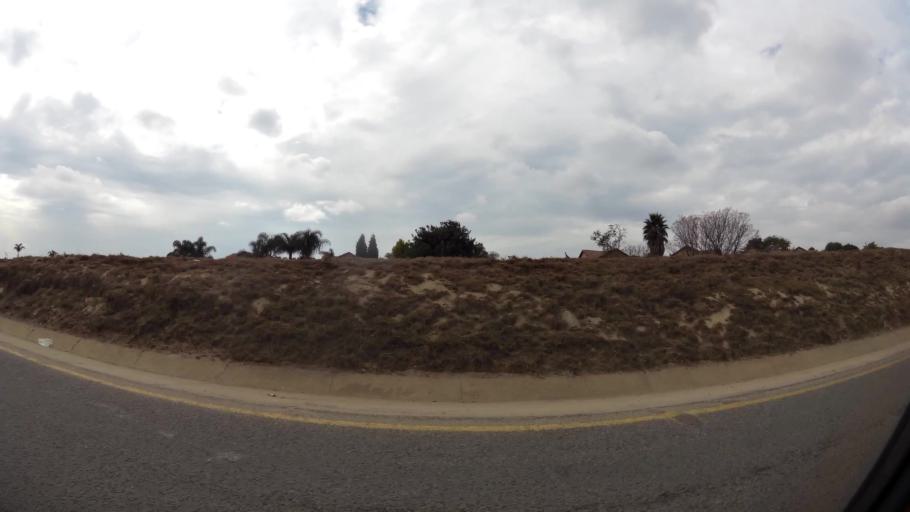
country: ZA
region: Gauteng
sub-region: West Rand District Municipality
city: Muldersdriseloop
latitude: -26.0699
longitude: 27.8510
